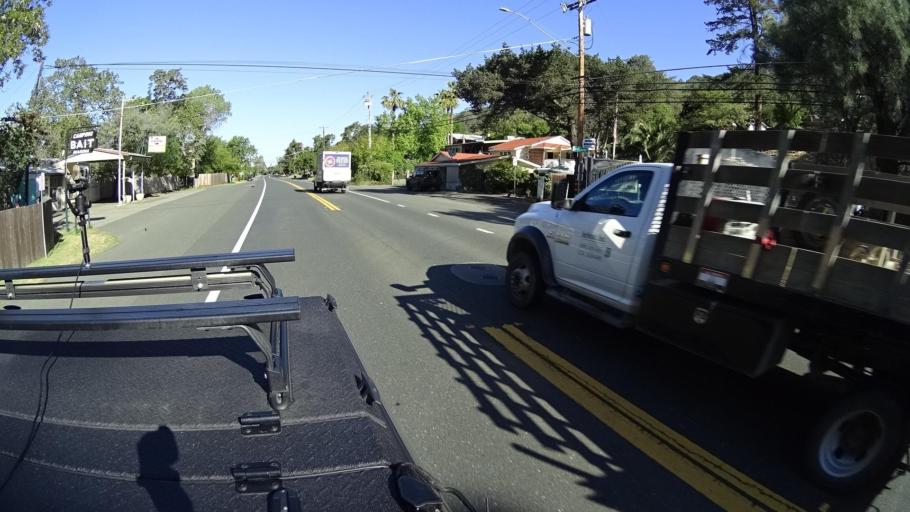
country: US
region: California
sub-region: Lake County
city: Clearlake Oaks
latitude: 39.0259
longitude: -122.7307
